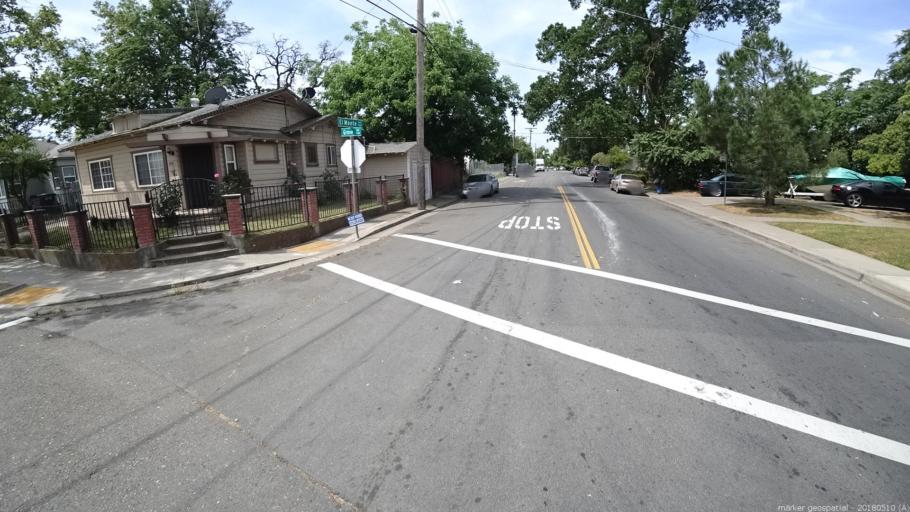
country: US
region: California
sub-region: Sacramento County
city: Sacramento
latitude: 38.6073
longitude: -121.4594
